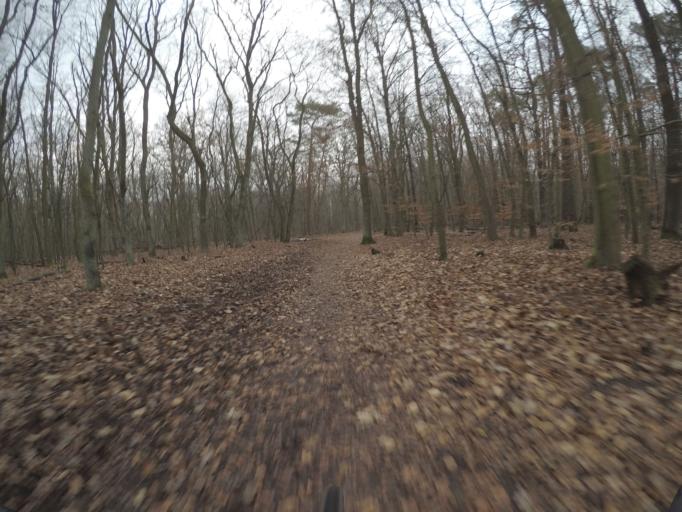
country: DE
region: Berlin
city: Grunau
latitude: 52.4168
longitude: 13.5977
